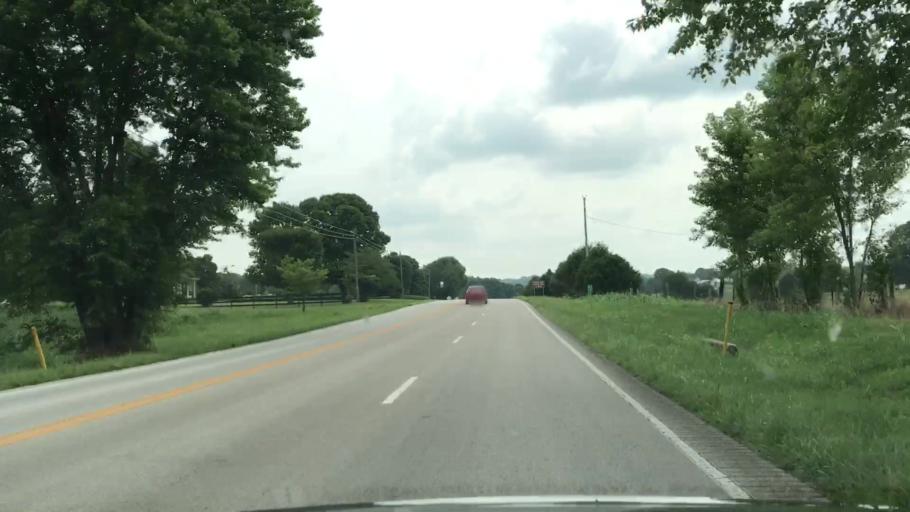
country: US
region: Kentucky
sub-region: Barren County
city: Cave City
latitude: 37.0918
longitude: -86.0855
